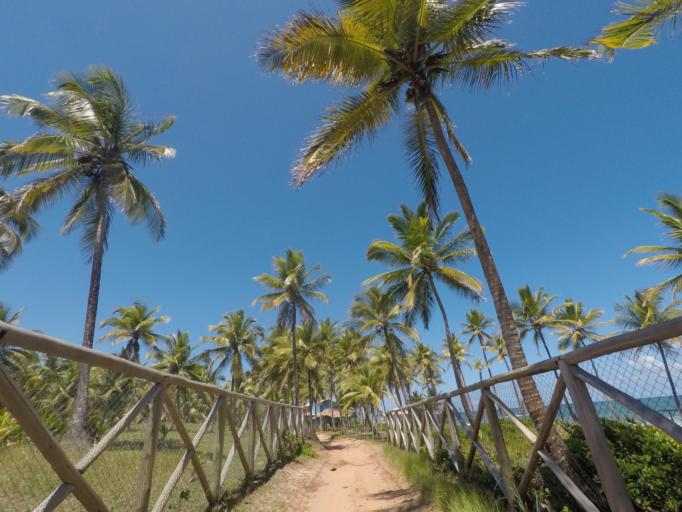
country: BR
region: Bahia
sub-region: Marau
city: Marau
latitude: -14.0183
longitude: -38.9455
